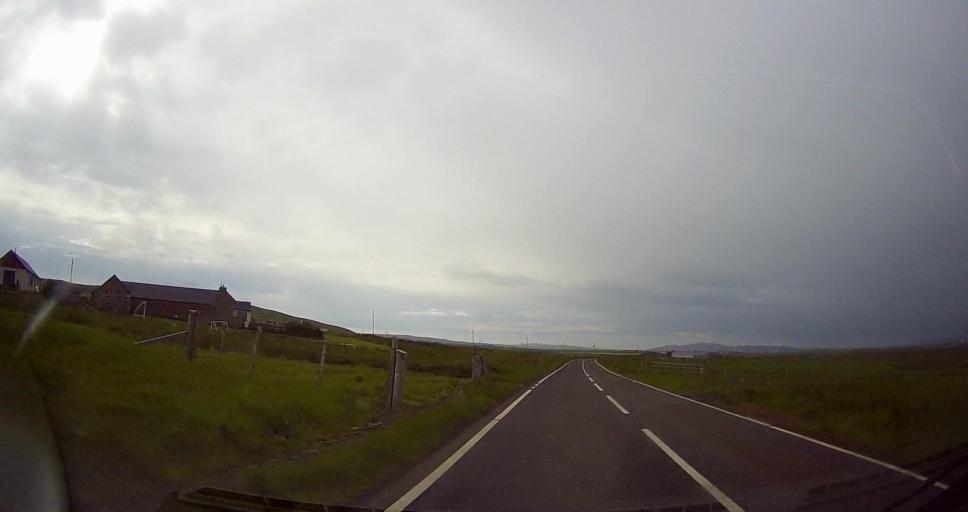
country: GB
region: Scotland
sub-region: Orkney Islands
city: Stromness
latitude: 59.0947
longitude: -3.2648
